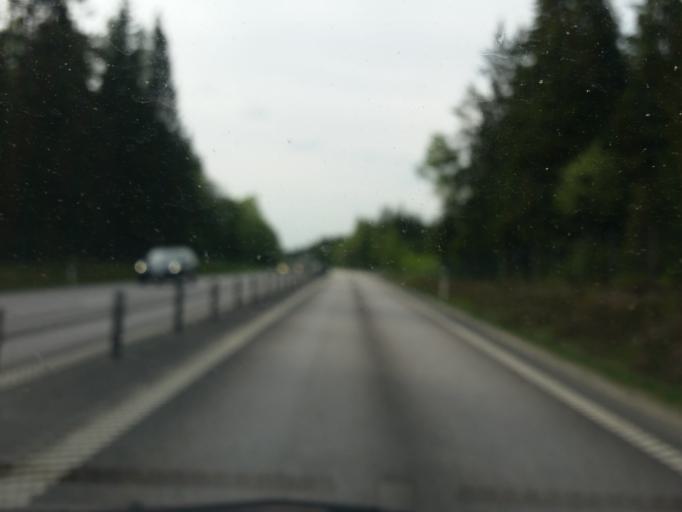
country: SE
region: Vaestra Goetaland
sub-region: Ulricehamns Kommun
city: Ulricehamn
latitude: 57.7909
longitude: 13.6306
